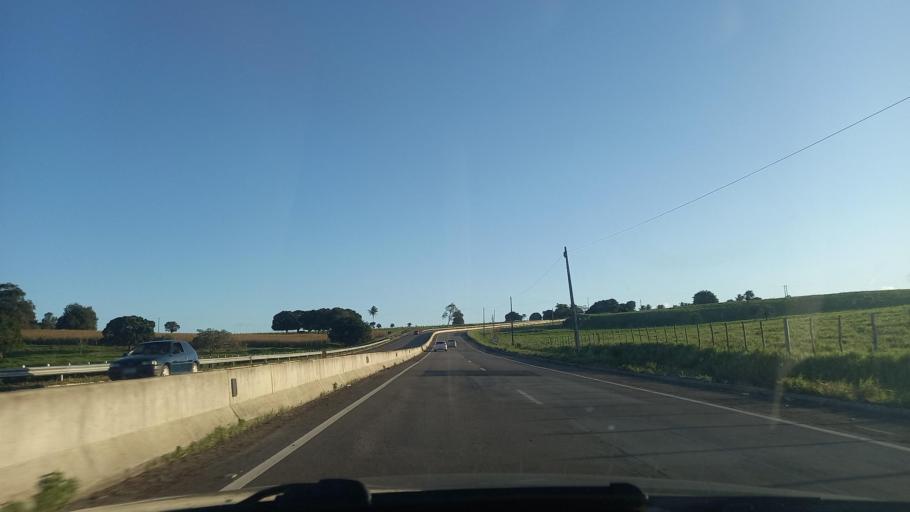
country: BR
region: Alagoas
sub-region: Limoeiro De Anadia
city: Limoeiro de Anadia
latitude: -9.7597
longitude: -36.5059
